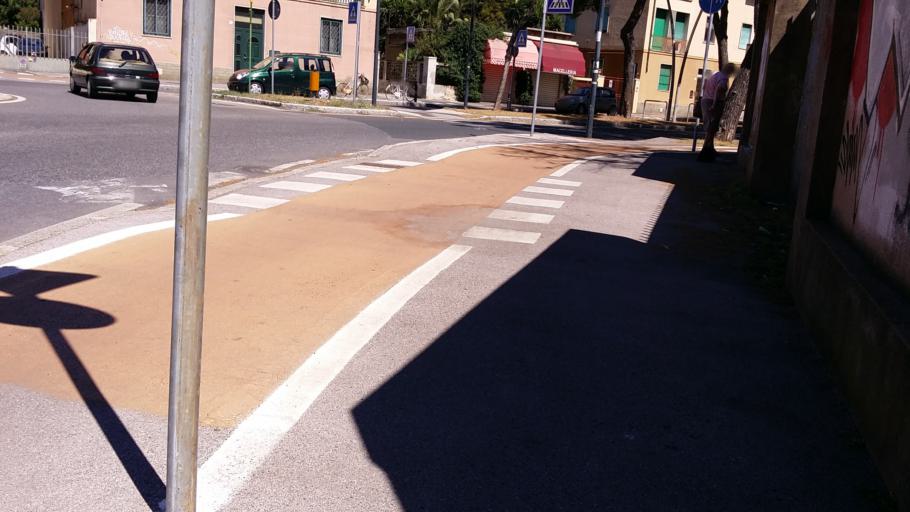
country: IT
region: Tuscany
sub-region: Provincia di Livorno
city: Livorno
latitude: 43.5298
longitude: 10.3142
